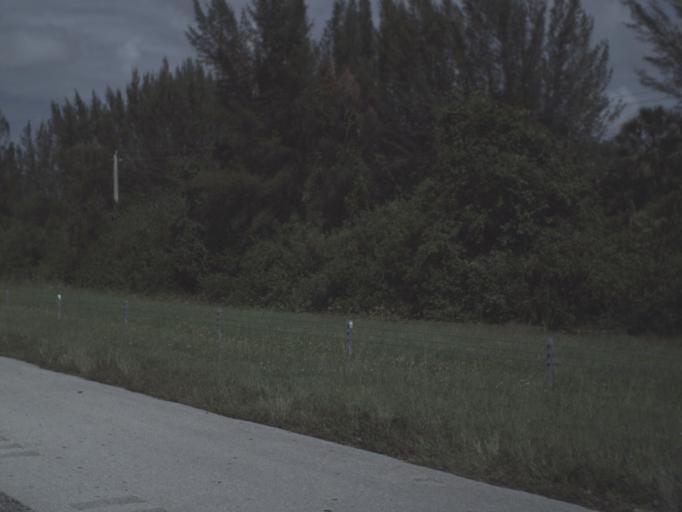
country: US
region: Florida
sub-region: Palm Beach County
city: Palm Beach Gardens
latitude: 26.8128
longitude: -80.1309
